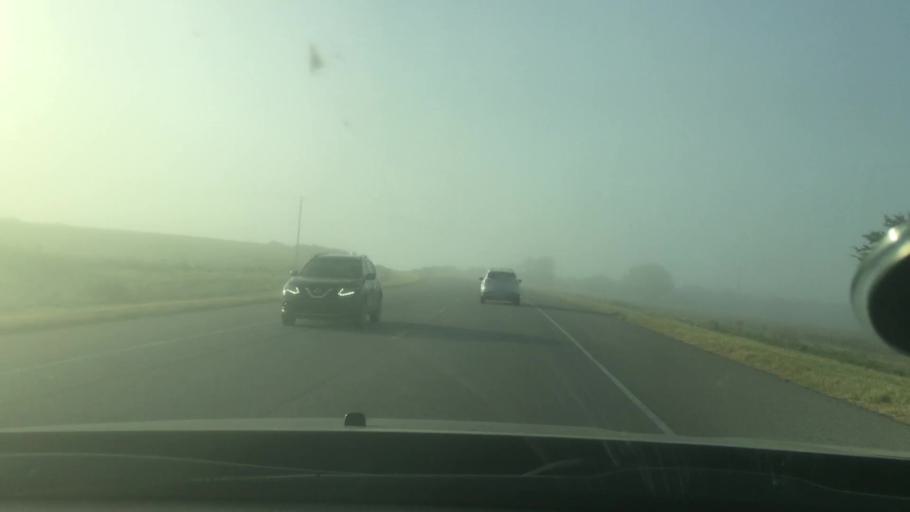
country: US
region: Oklahoma
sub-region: Pontotoc County
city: Ada
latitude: 34.6846
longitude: -96.5907
